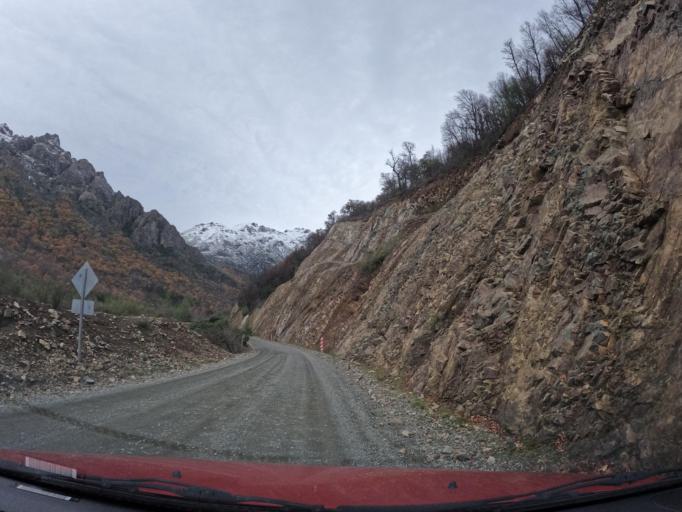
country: CL
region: Maule
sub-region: Provincia de Linares
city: Colbun
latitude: -35.8612
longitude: -71.1275
